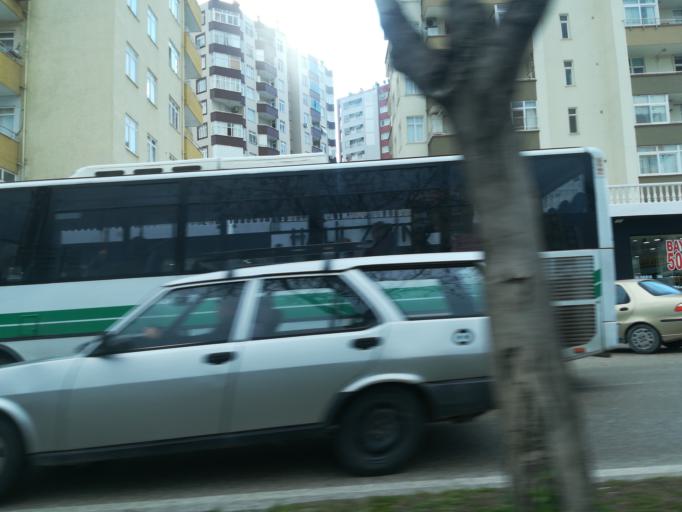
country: TR
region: Adana
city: Adana
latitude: 37.0407
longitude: 35.3021
